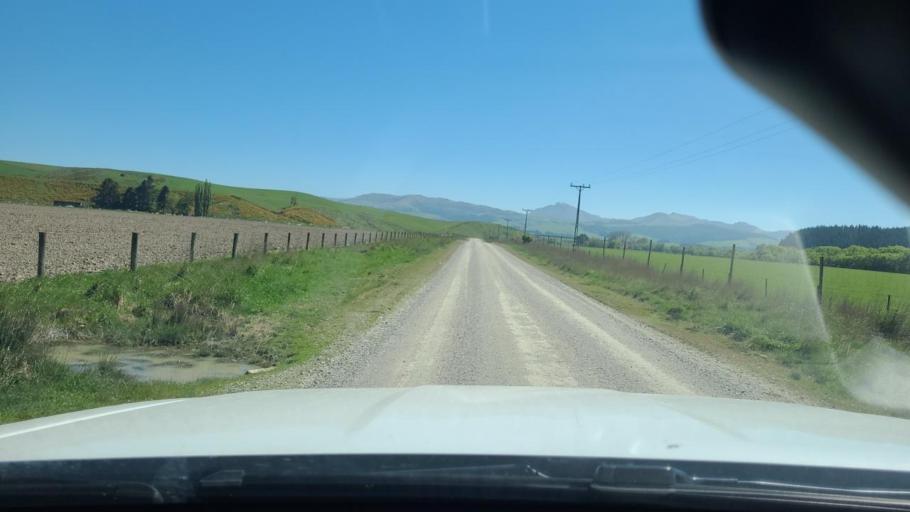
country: NZ
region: Southland
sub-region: Gore District
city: Gore
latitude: -45.7405
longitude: 168.8166
